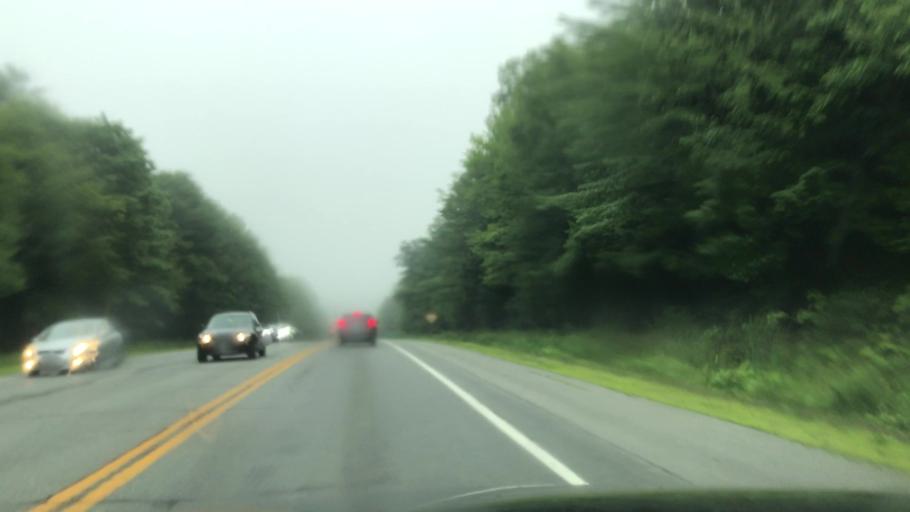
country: US
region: Maine
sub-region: Lincoln County
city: Waldoboro
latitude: 44.0998
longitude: -69.3970
